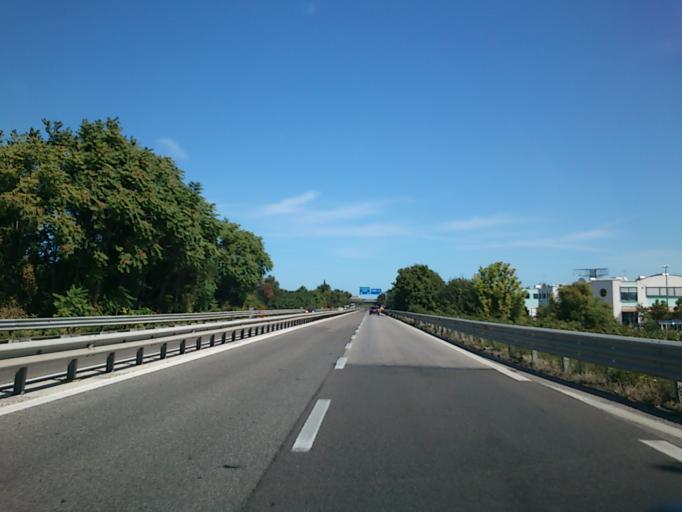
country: IT
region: The Marches
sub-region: Provincia di Pesaro e Urbino
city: Bellocchi
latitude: 43.8017
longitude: 13.0117
